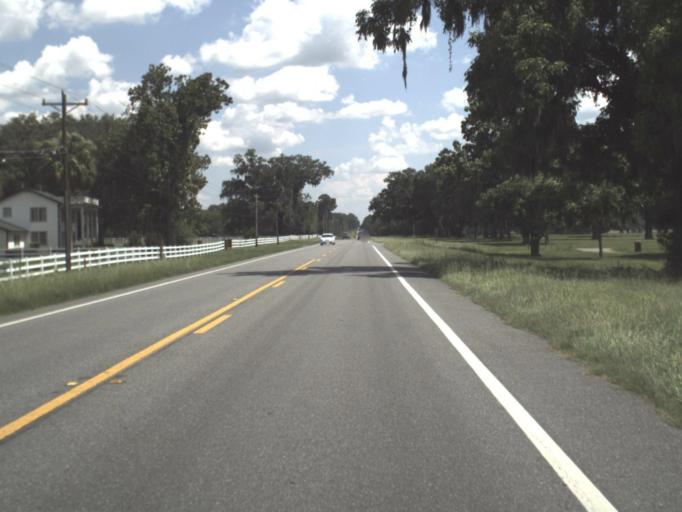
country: US
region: Florida
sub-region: Columbia County
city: Watertown
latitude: 30.0814
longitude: -82.6013
